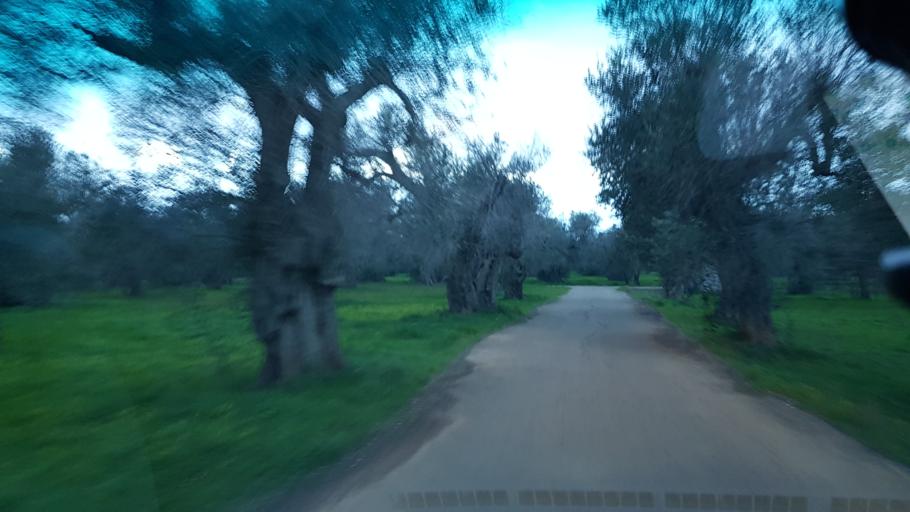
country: IT
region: Apulia
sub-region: Provincia di Brindisi
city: Torchiarolo
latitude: 40.4908
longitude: 18.0580
